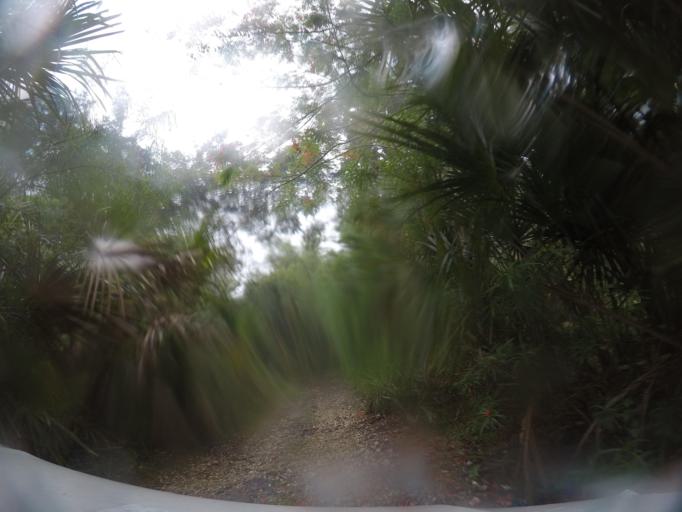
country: TL
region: Baucau
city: Venilale
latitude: -8.6411
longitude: 126.4349
